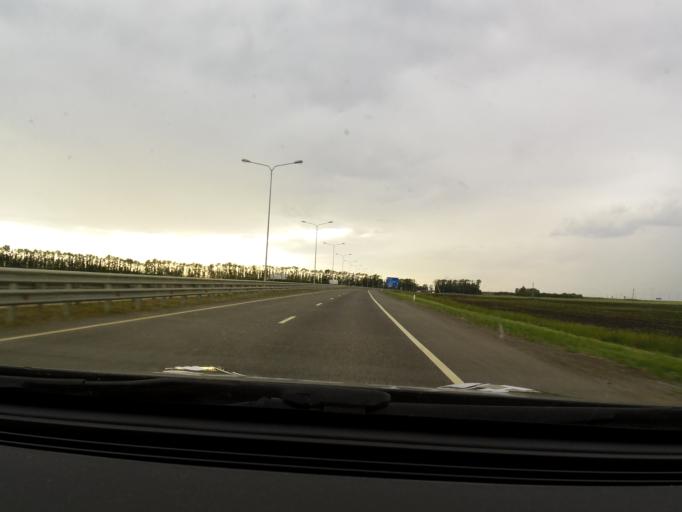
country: RU
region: Bashkortostan
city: Kushnarenkovo
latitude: 55.0651
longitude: 55.3311
